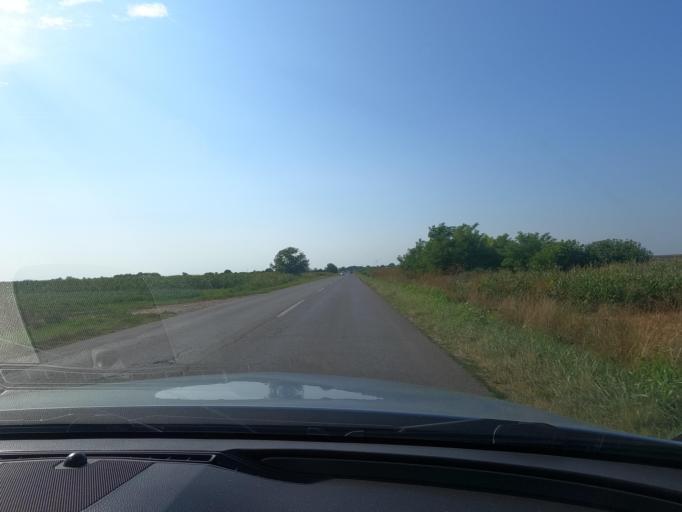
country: RS
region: Autonomna Pokrajina Vojvodina
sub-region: Juznobacki Okrug
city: Kovilj
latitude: 45.2847
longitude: 19.9712
